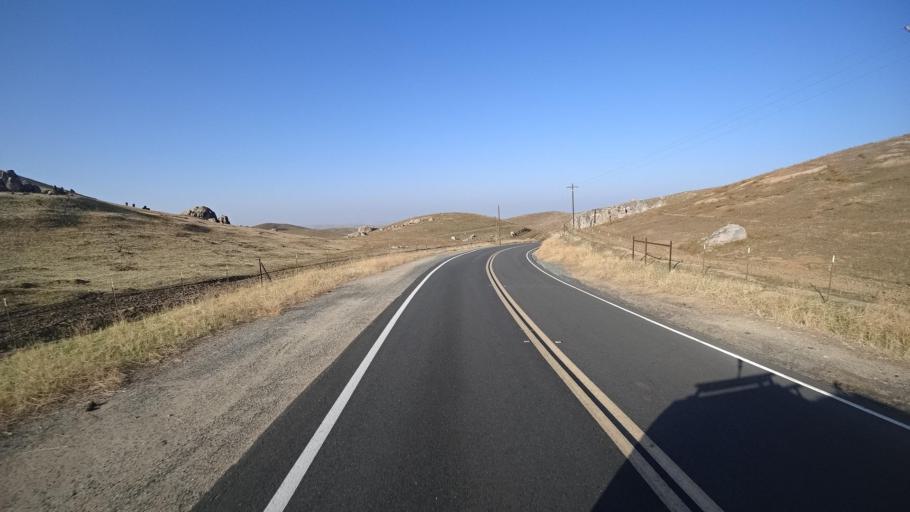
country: US
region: California
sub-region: Tulare County
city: Richgrove
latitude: 35.7425
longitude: -118.8987
